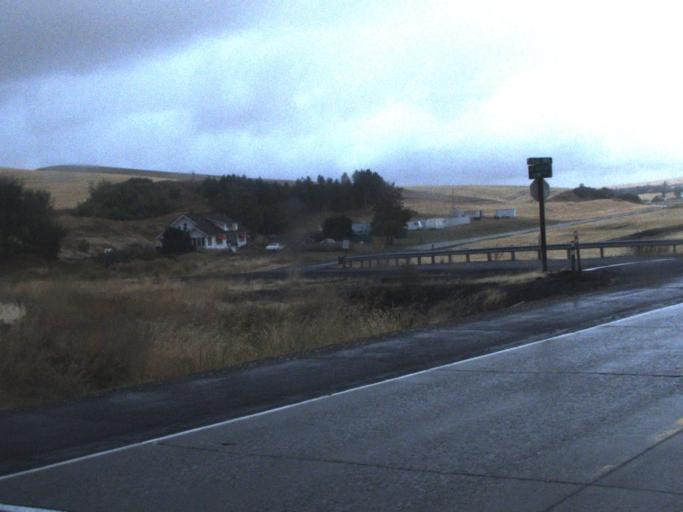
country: US
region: Washington
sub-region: Whitman County
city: Colfax
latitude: 47.1042
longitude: -117.3790
